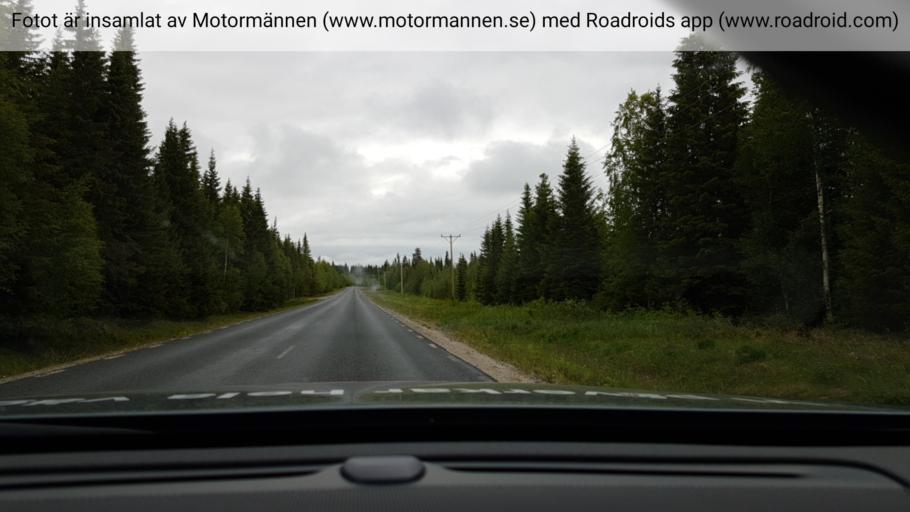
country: SE
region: Vaesterbotten
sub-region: Lycksele Kommun
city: Soderfors
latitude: 64.3782
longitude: 17.9819
